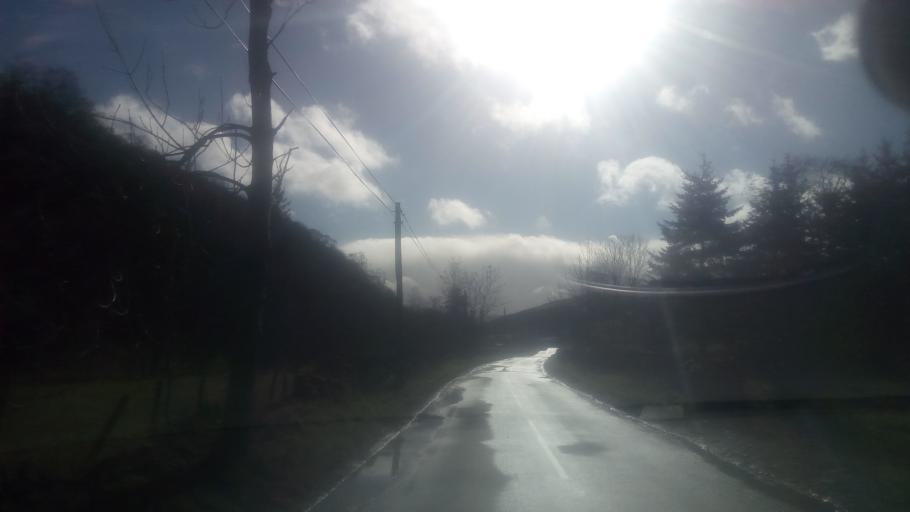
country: GB
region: Scotland
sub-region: The Scottish Borders
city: Innerleithen
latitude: 55.5840
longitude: -3.0840
